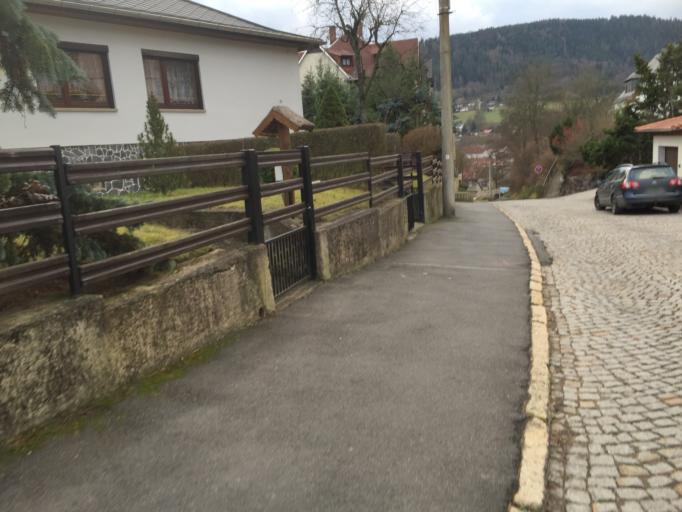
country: DE
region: Thuringia
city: Bad Blankenburg
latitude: 50.6852
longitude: 11.2683
